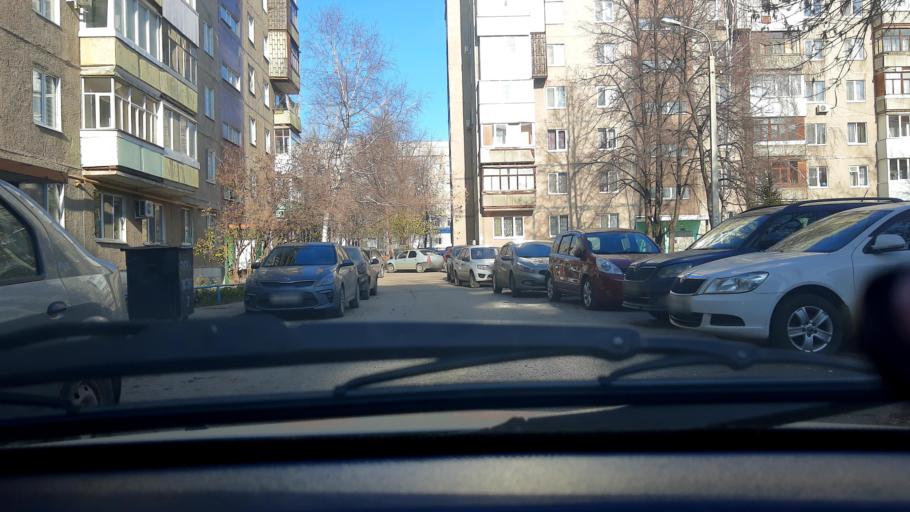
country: RU
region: Bashkortostan
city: Ufa
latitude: 54.7070
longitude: 56.0064
